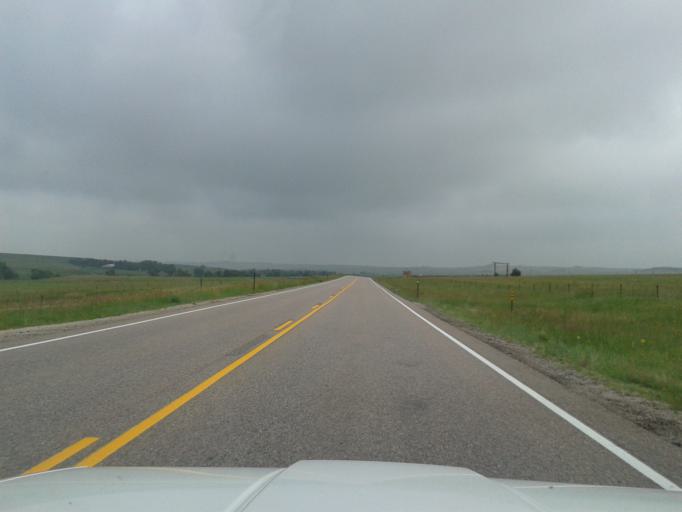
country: US
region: Colorado
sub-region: El Paso County
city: Woodmoor
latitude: 39.2112
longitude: -104.7114
